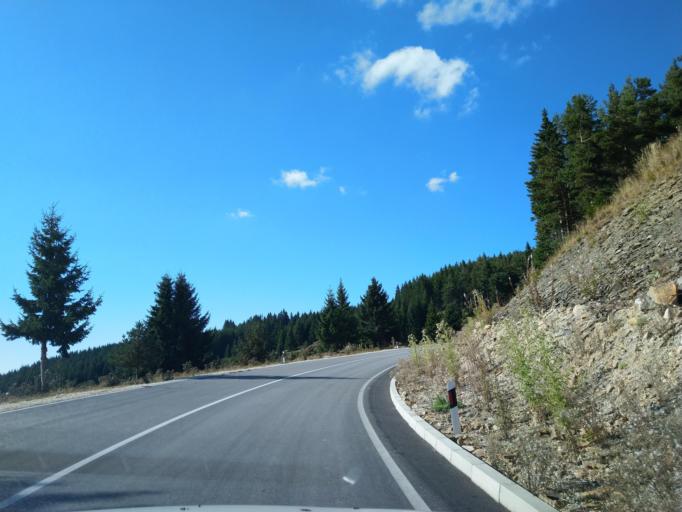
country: RS
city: Sokolovica
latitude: 43.3083
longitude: 20.3013
